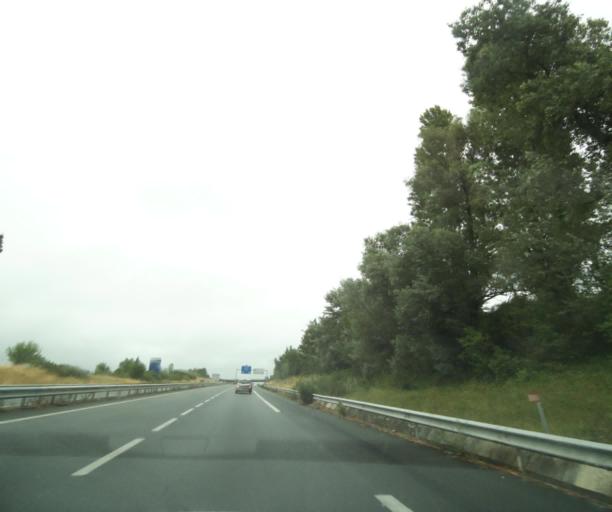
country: FR
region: Midi-Pyrenees
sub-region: Departement de la Haute-Garonne
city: Montastruc-la-Conseillere
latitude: 43.7385
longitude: 1.5875
